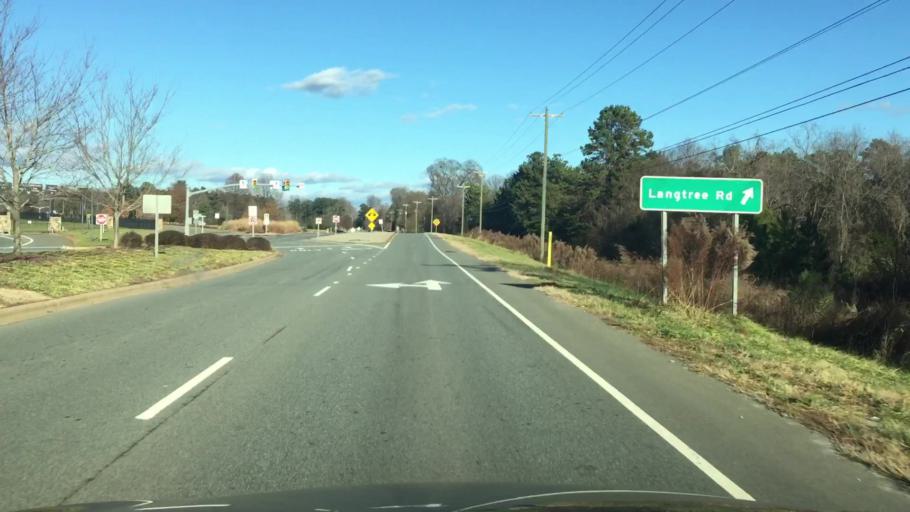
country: US
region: North Carolina
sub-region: Gaston County
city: Davidson
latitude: 35.5336
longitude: -80.8563
